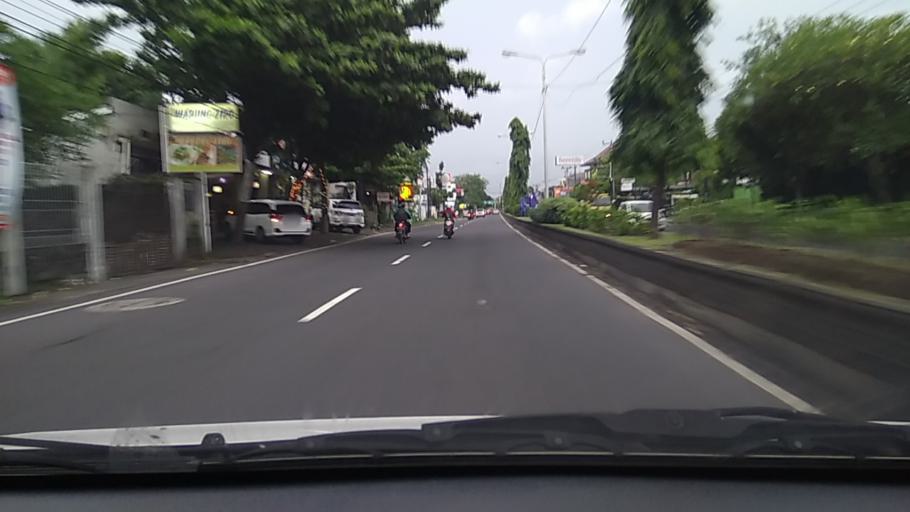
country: ID
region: Bali
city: Banjar Taman
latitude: -8.6868
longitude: 115.2587
